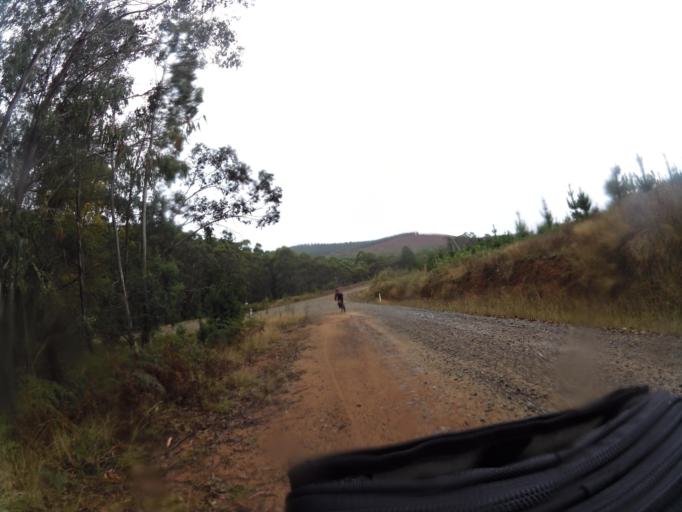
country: AU
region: New South Wales
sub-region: Greater Hume Shire
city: Holbrook
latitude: -36.2102
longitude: 147.5725
